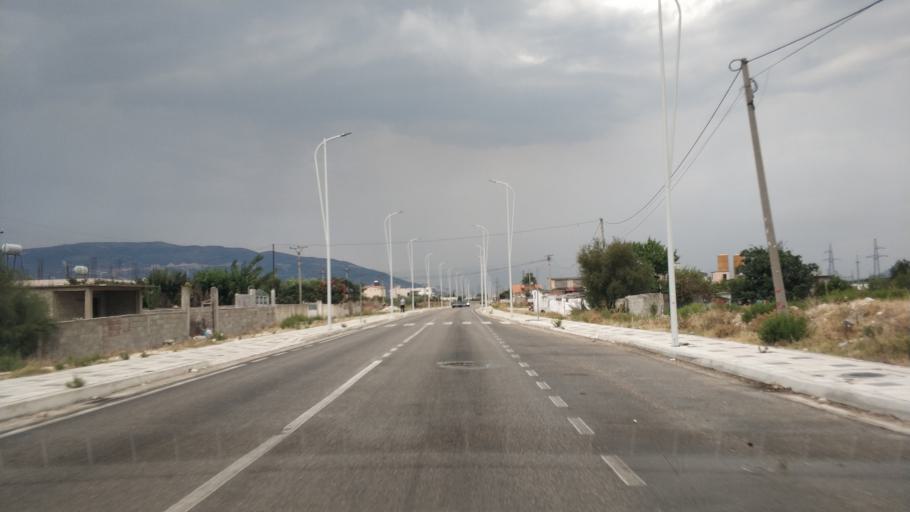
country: AL
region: Vlore
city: Vlore
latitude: 40.4795
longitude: 19.4669
